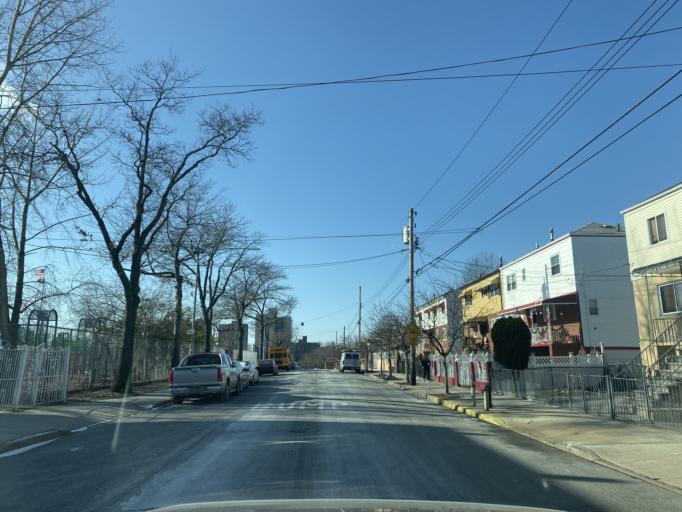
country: US
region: New York
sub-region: Bronx
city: The Bronx
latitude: 40.8239
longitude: -73.8498
